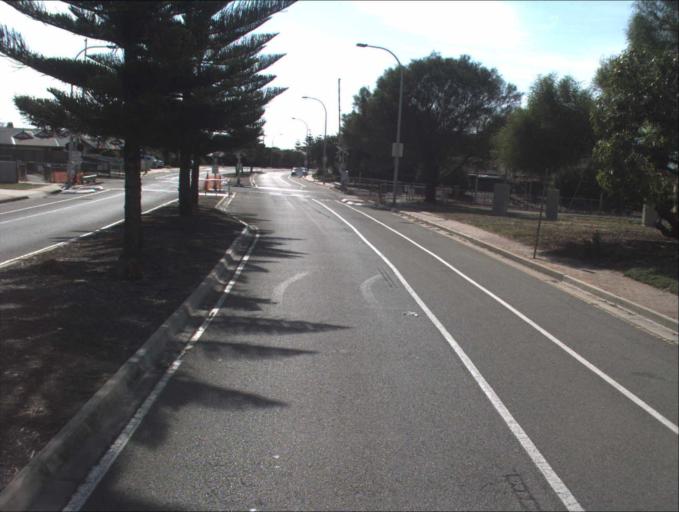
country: AU
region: South Australia
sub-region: Port Adelaide Enfield
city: Birkenhead
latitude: -34.7923
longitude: 138.4985
